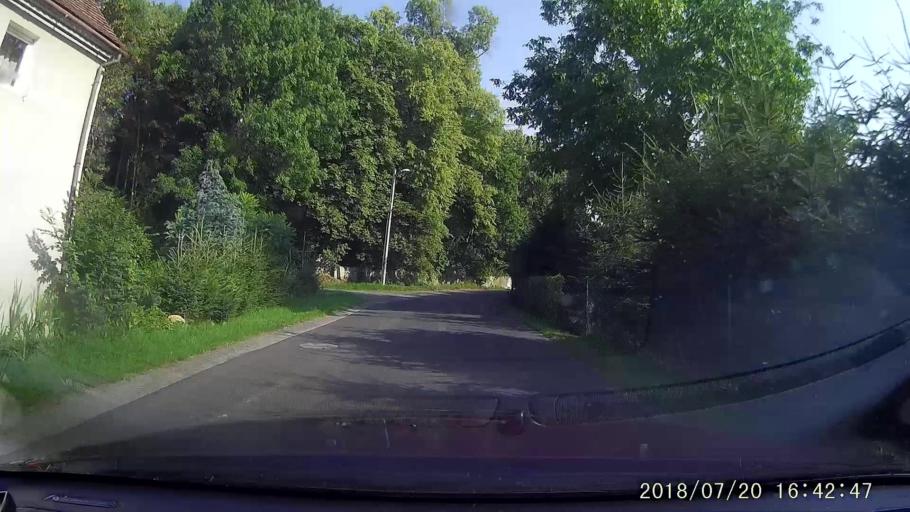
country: PL
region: Lower Silesian Voivodeship
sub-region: Powiat lubanski
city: Siekierczyn
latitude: 51.0735
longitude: 15.1561
